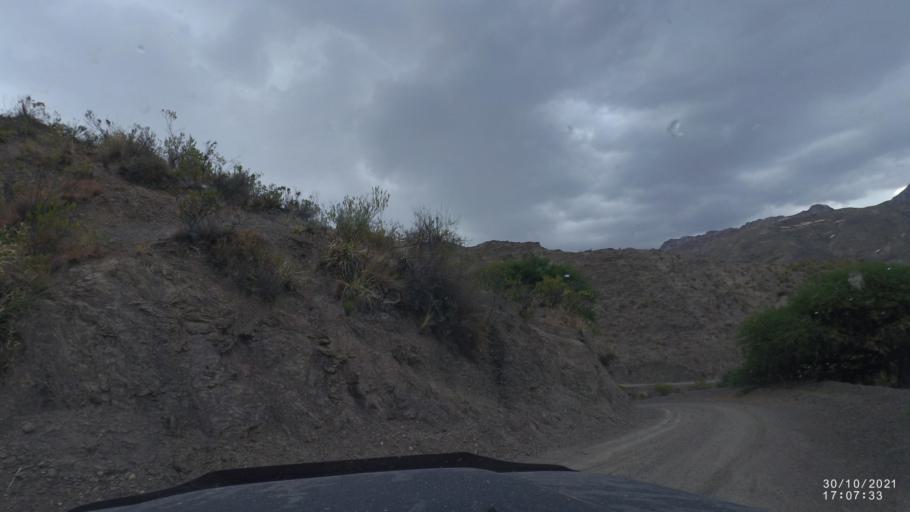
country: BO
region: Cochabamba
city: Colchani
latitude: -17.5631
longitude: -66.6252
